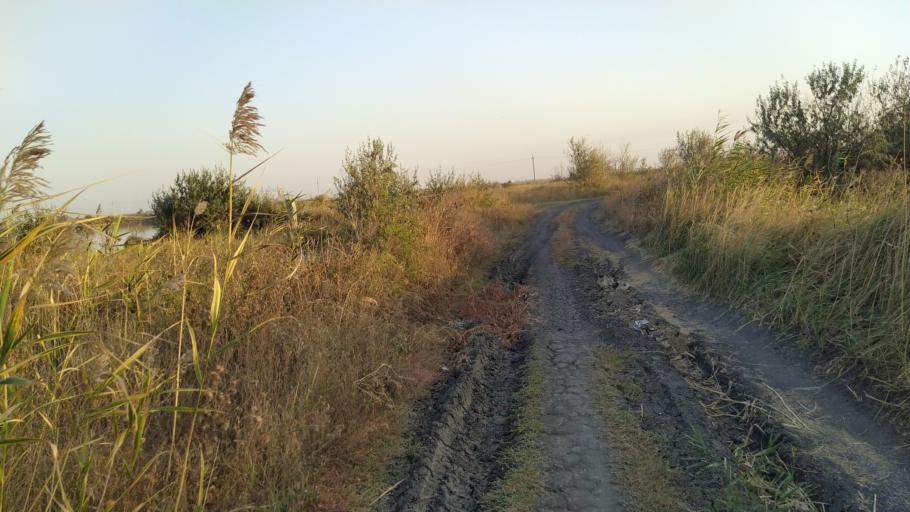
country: RU
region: Rostov
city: Kuleshovka
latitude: 47.1398
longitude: 39.6448
